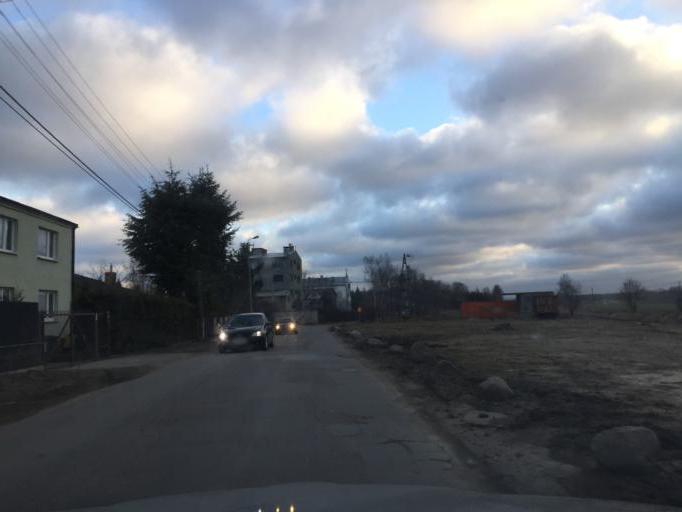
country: PL
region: Pomeranian Voivodeship
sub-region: Powiat kartuski
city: Chwaszczyno
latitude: 54.4138
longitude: 18.4462
